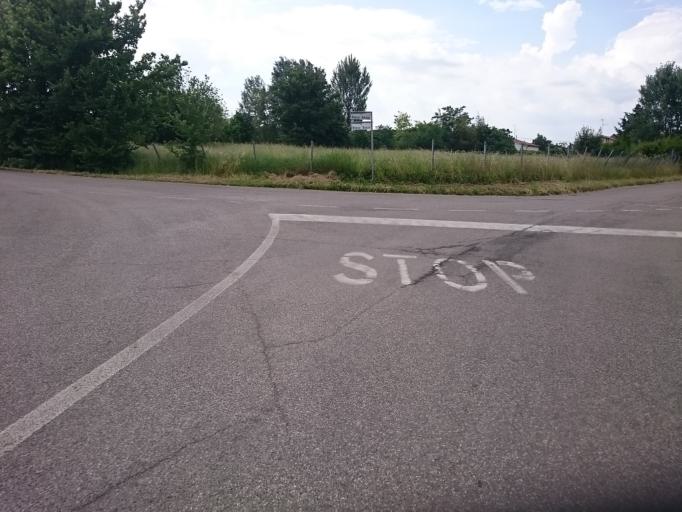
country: IT
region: Veneto
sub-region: Provincia di Padova
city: Megliadino San Vitale
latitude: 45.2009
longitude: 11.5377
